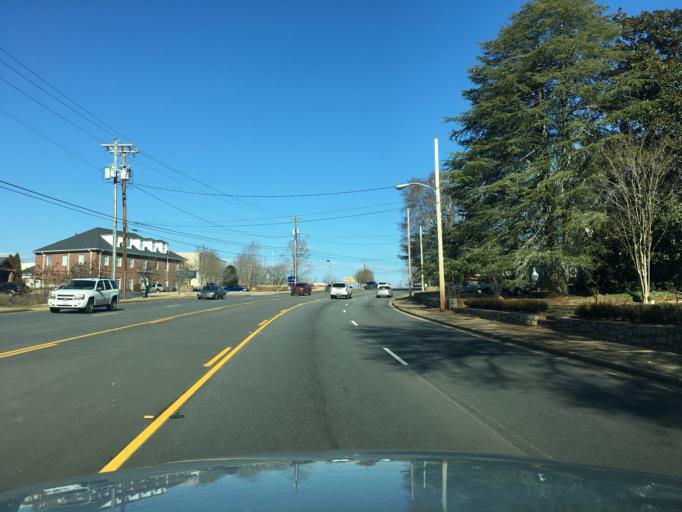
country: US
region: South Carolina
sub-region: Pickens County
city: Pickens
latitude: 34.8788
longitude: -82.7016
